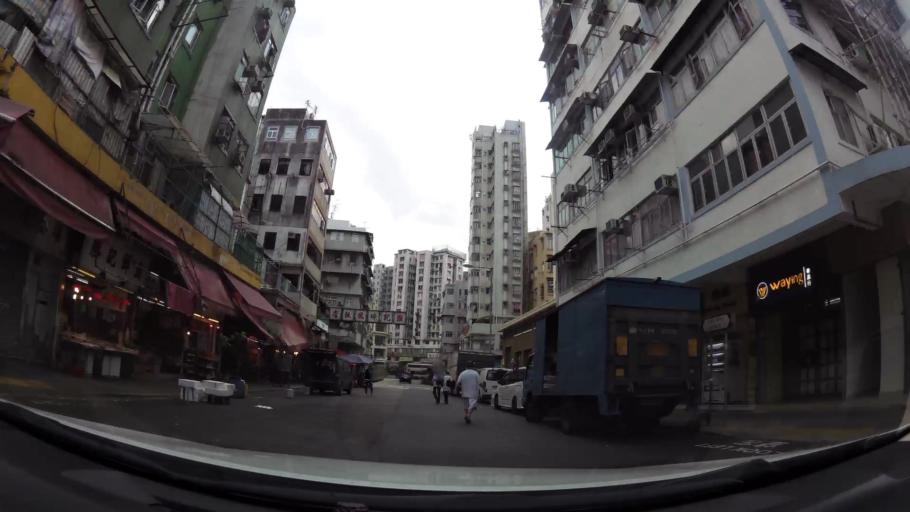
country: HK
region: Sham Shui Po
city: Sham Shui Po
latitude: 22.3258
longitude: 114.1657
